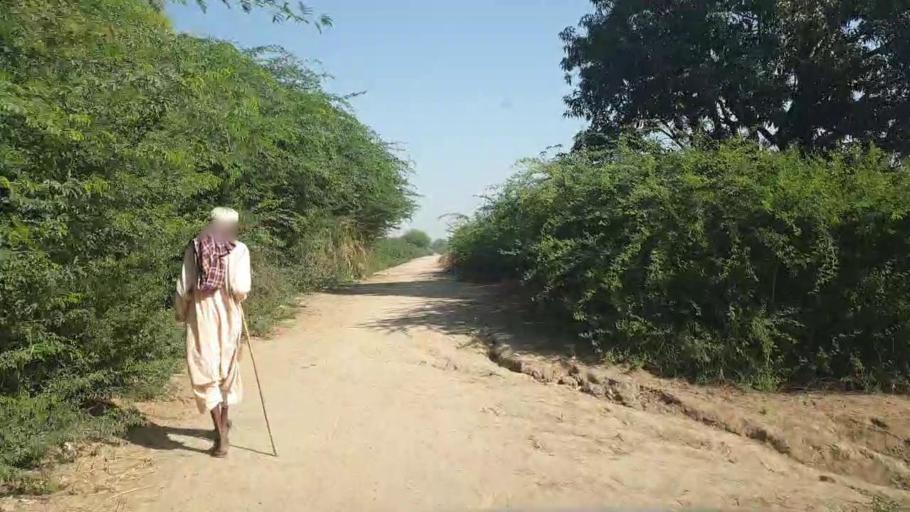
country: PK
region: Sindh
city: Talhar
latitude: 24.7791
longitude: 68.8064
